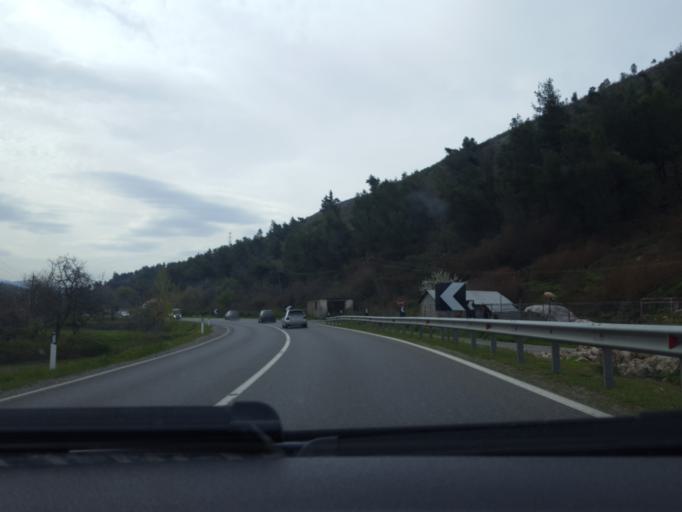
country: AL
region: Lezhe
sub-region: Rrethi i Lezhes
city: Balldreni i Ri
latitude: 41.8014
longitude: 19.6303
